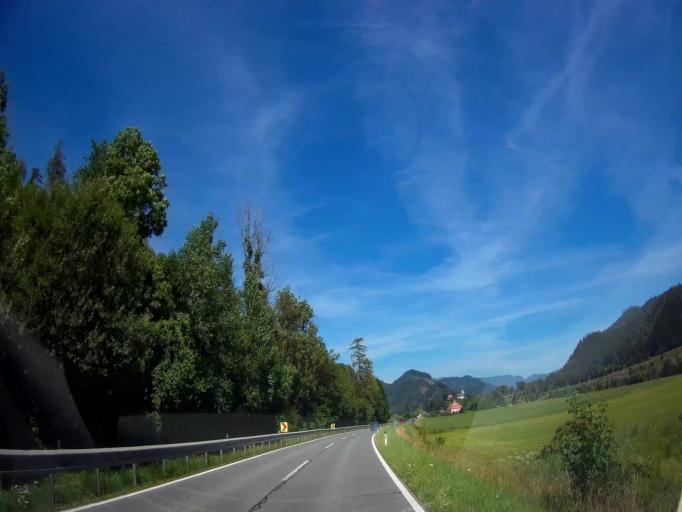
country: AT
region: Carinthia
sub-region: Politischer Bezirk Sankt Veit an der Glan
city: Althofen
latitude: 46.8822
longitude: 14.4463
